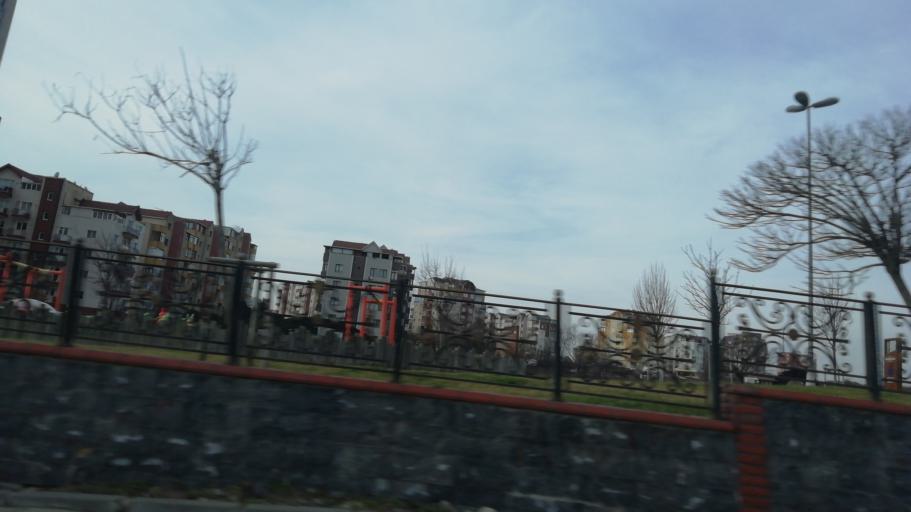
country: TR
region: Istanbul
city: Basaksehir
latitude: 41.1091
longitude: 28.7956
